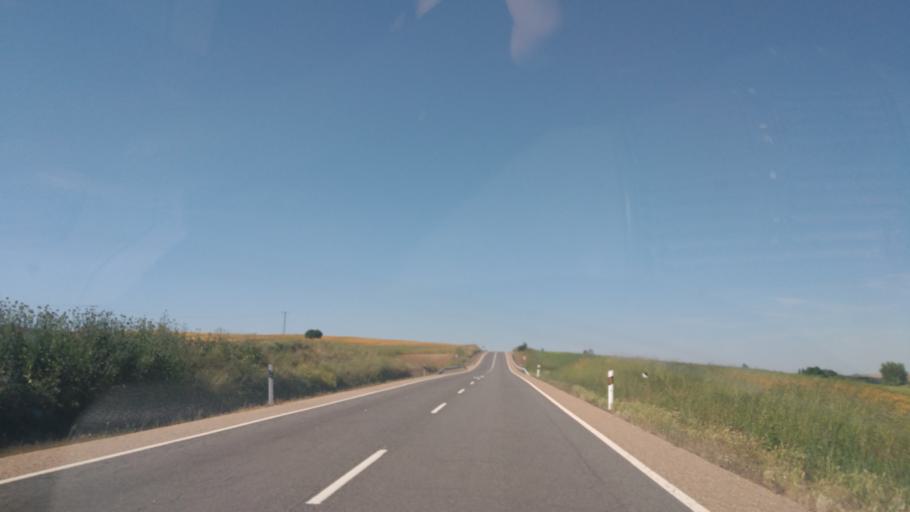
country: ES
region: Castille and Leon
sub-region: Provincia de Zamora
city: Corrales
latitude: 41.3341
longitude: -5.7323
